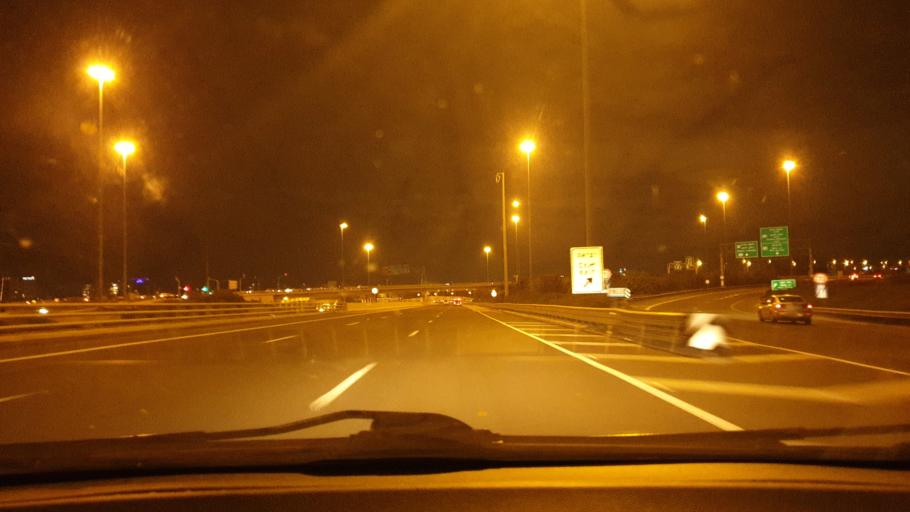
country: IL
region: Central District
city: Ness Ziona
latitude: 31.9363
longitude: 34.8165
